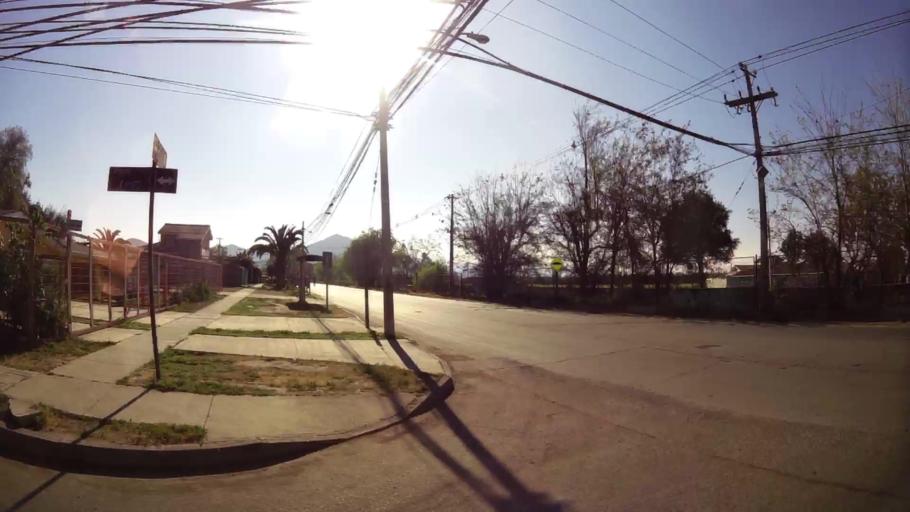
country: CL
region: Santiago Metropolitan
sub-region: Provincia de Santiago
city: Lo Prado
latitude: -33.4881
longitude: -70.7787
